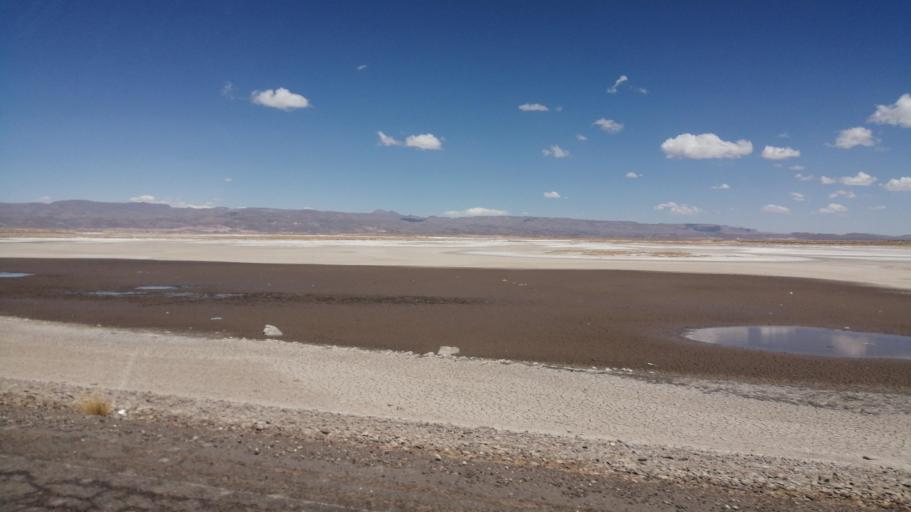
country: BO
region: Oruro
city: Challapata
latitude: -19.1879
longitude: -66.8449
